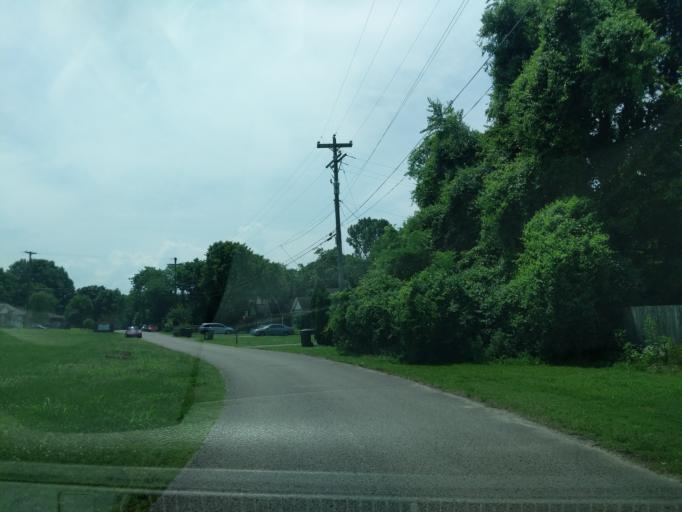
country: US
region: Tennessee
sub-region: Davidson County
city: Lakewood
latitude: 36.2293
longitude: -86.6353
